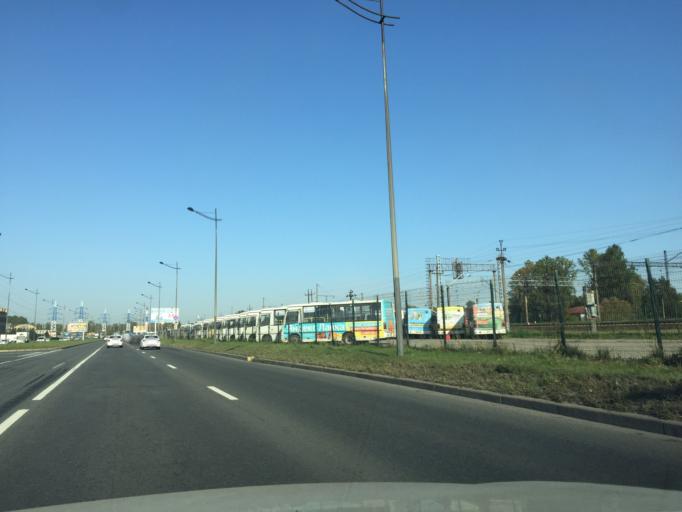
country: RU
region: St.-Petersburg
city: Kupchino
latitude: 59.8824
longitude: 30.3464
